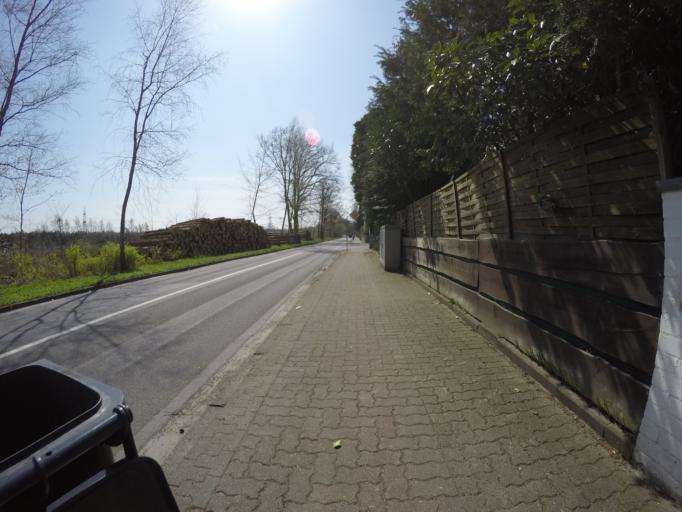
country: DE
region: Schleswig-Holstein
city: Quickborn
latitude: 53.7254
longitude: 9.9279
